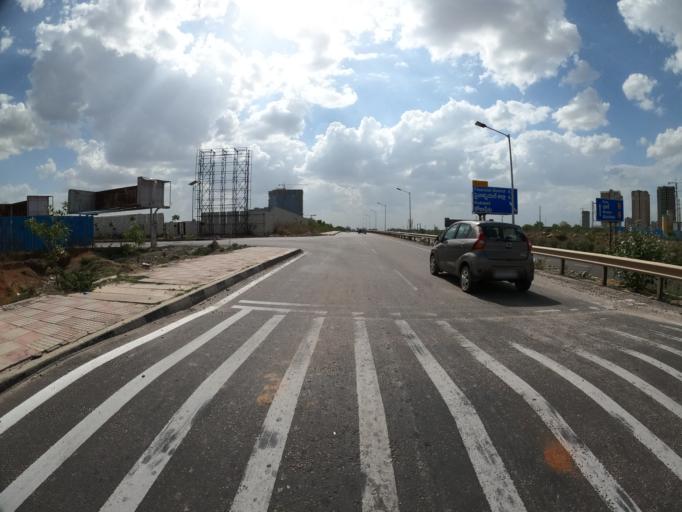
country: IN
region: Telangana
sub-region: Medak
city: Serilingampalle
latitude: 17.4024
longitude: 78.3389
